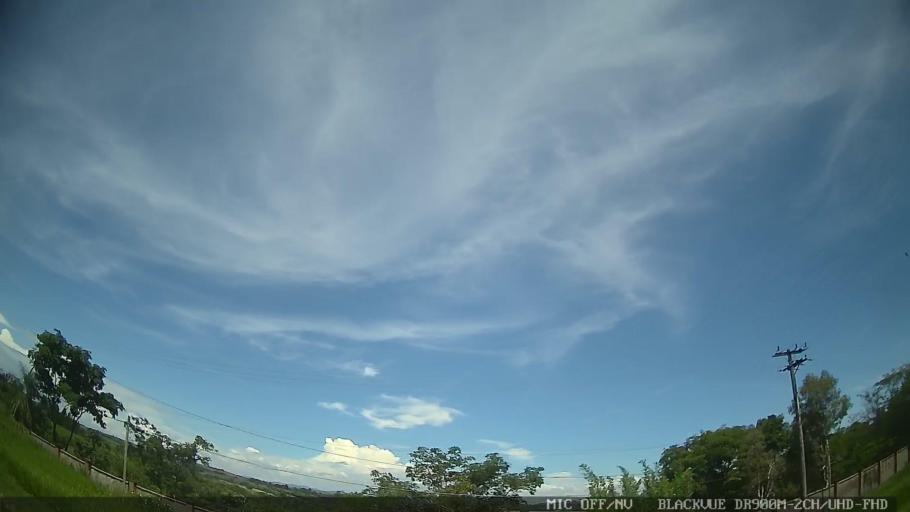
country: BR
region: Sao Paulo
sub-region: Jaguariuna
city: Jaguariuna
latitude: -22.6432
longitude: -47.0058
